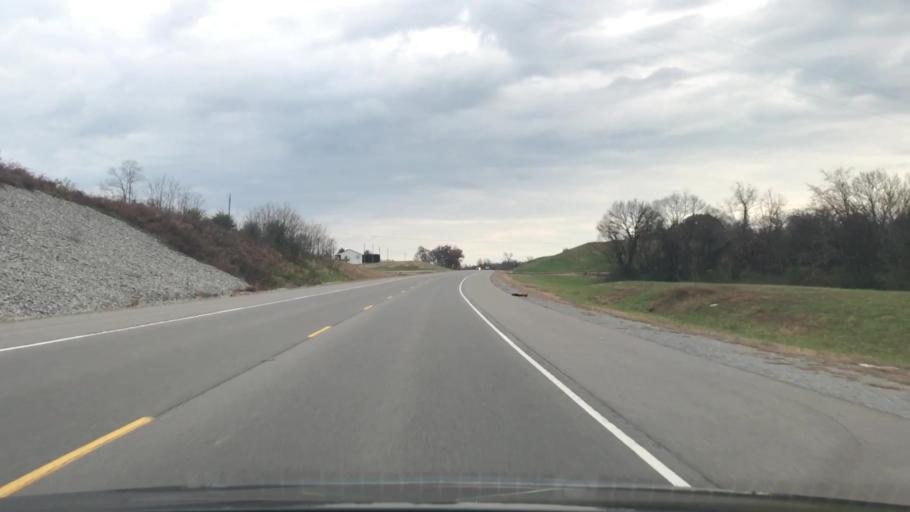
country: US
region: Tennessee
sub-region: Trousdale County
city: Hartsville
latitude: 36.3317
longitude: -86.1728
